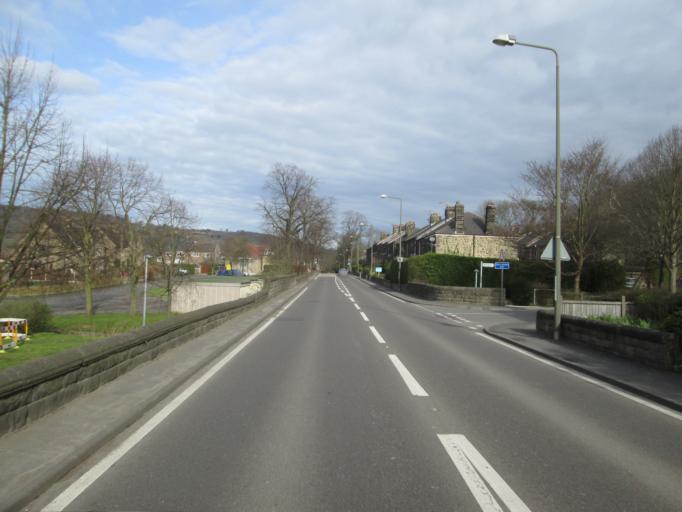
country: GB
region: England
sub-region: Derbyshire
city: Matlock
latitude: 53.1657
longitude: -1.5968
